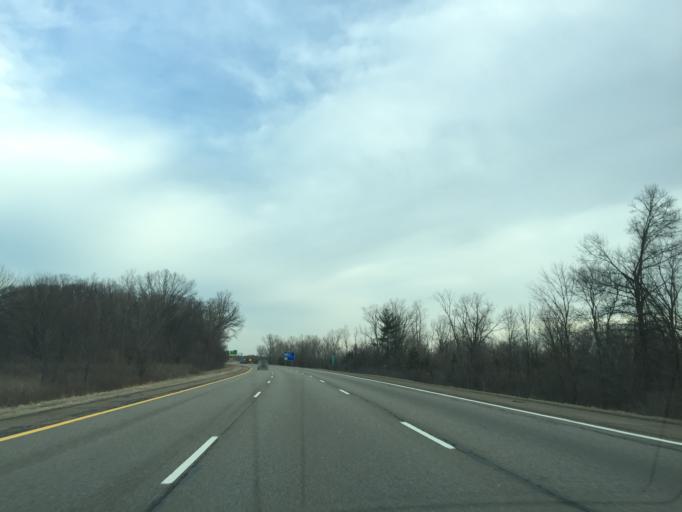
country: US
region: Michigan
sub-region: Berrien County
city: New Buffalo
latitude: 41.7932
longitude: -86.7111
